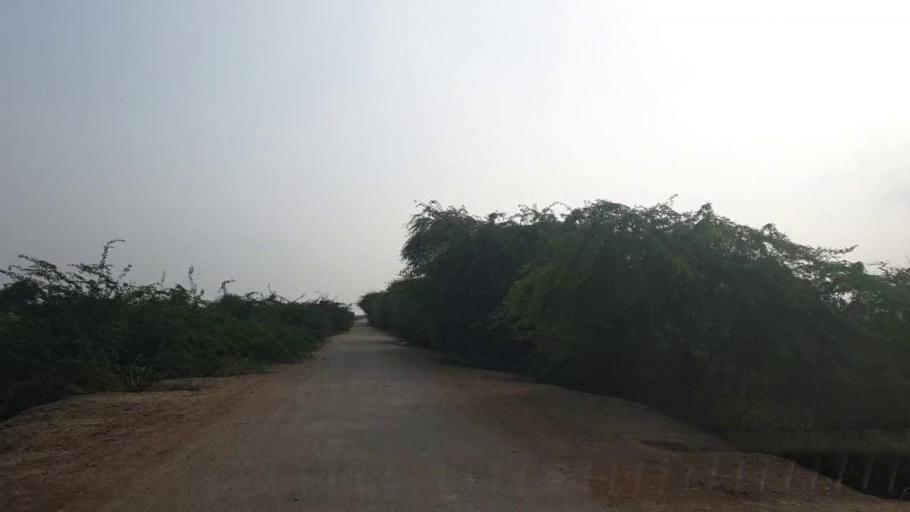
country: PK
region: Sindh
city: Badin
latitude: 24.6352
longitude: 68.6925
